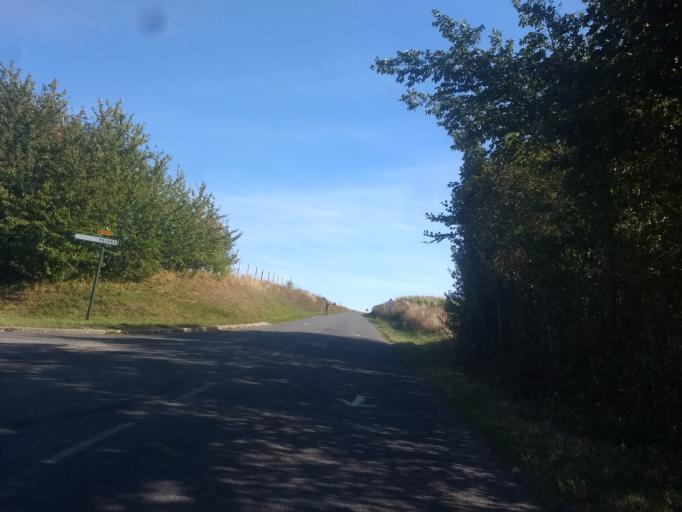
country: FR
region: Nord-Pas-de-Calais
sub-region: Departement du Pas-de-Calais
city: Roeux
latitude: 50.2876
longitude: 2.8995
